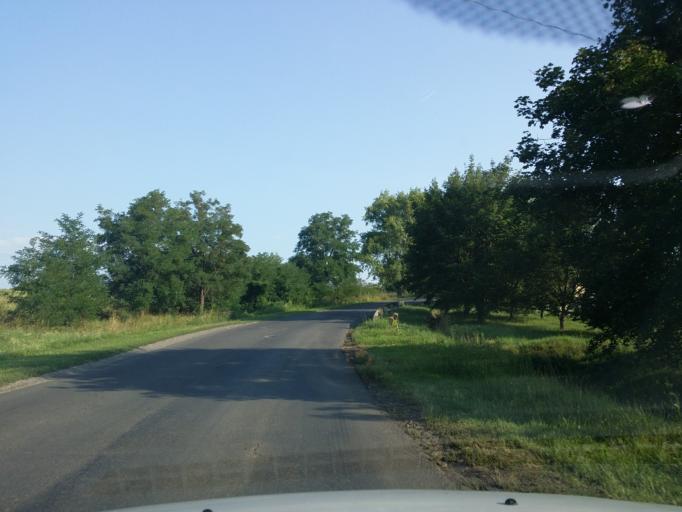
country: HU
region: Borsod-Abauj-Zemplen
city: Encs
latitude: 48.3752
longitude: 21.2152
